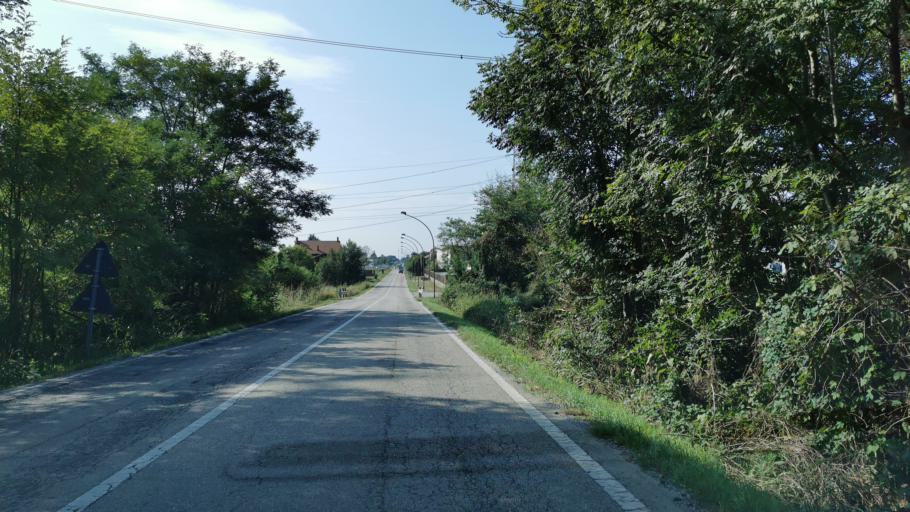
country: IT
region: Piedmont
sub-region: Provincia di Torino
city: Leini
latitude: 45.2071
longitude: 7.7283
